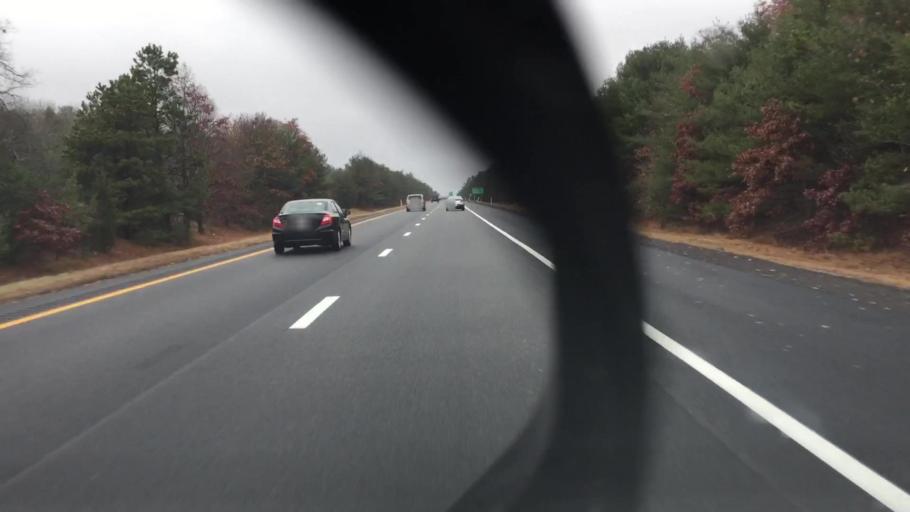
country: US
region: Massachusetts
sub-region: Plymouth County
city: West Wareham
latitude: 41.7872
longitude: -70.7390
